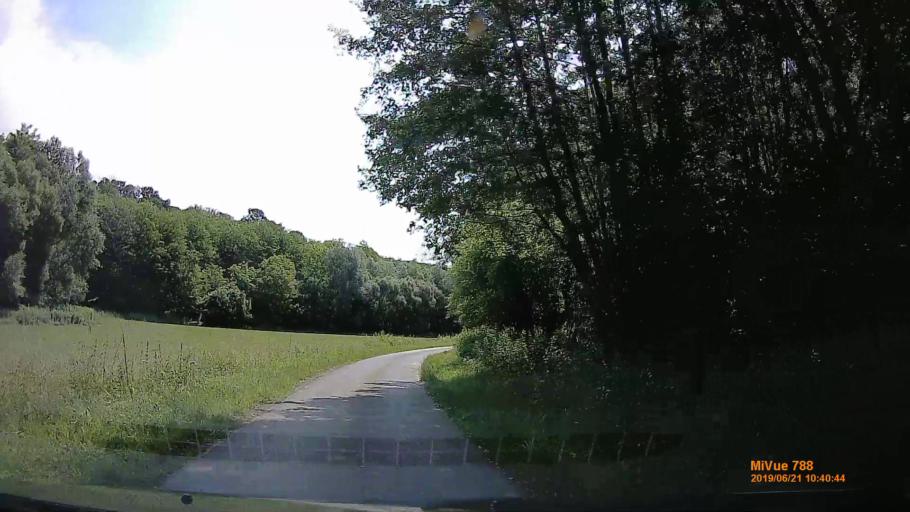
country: HU
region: Baranya
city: Buekkoesd
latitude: 46.1356
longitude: 17.9987
